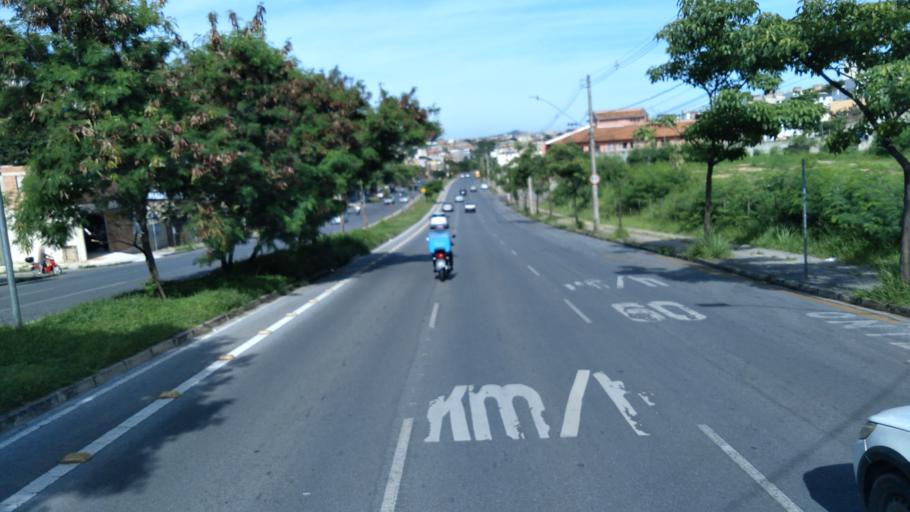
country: BR
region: Minas Gerais
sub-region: Belo Horizonte
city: Belo Horizonte
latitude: -19.9008
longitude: -43.9943
